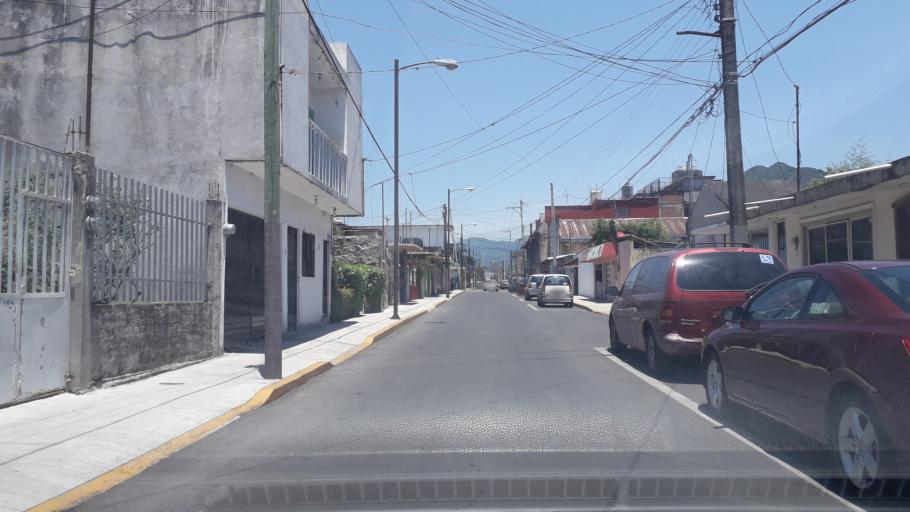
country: MX
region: Veracruz
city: Jalapilla
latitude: 18.8398
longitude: -97.0899
